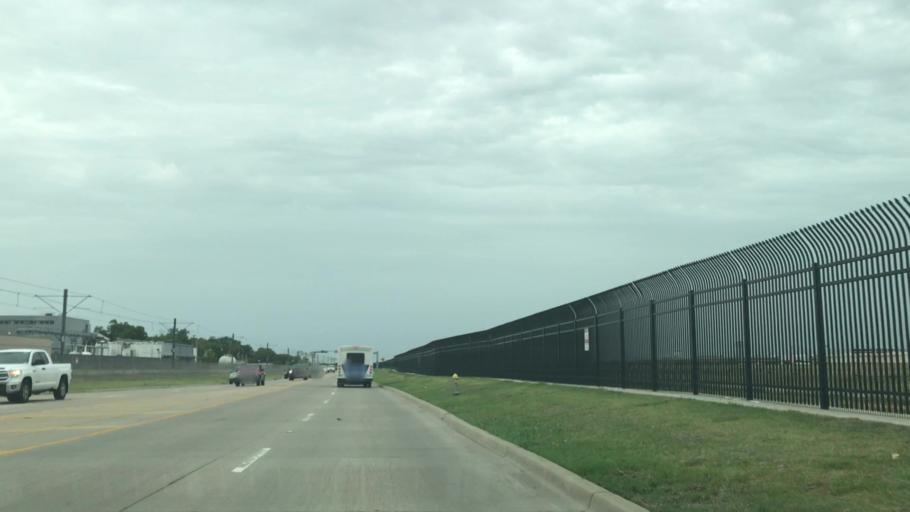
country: US
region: Texas
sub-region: Dallas County
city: University Park
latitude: 32.8319
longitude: -96.8432
